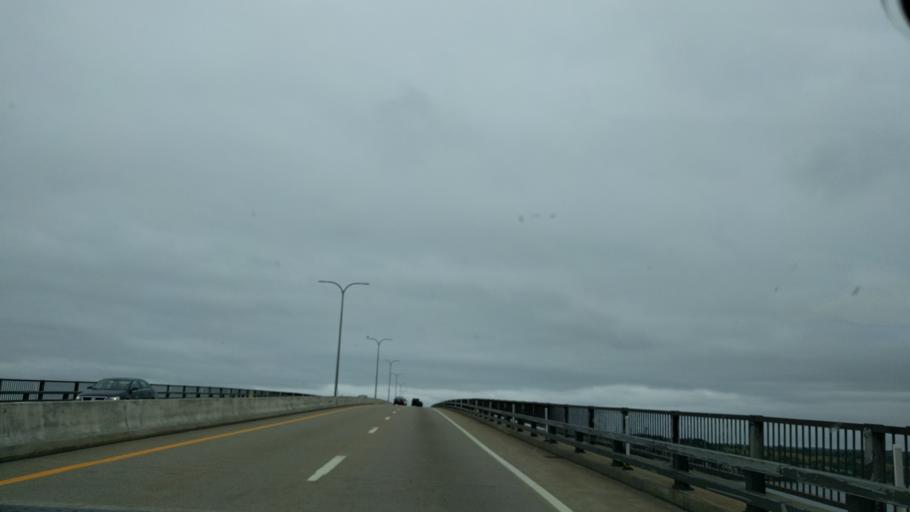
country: US
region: Rhode Island
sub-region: Newport County
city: Jamestown
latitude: 41.5280
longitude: -71.4009
